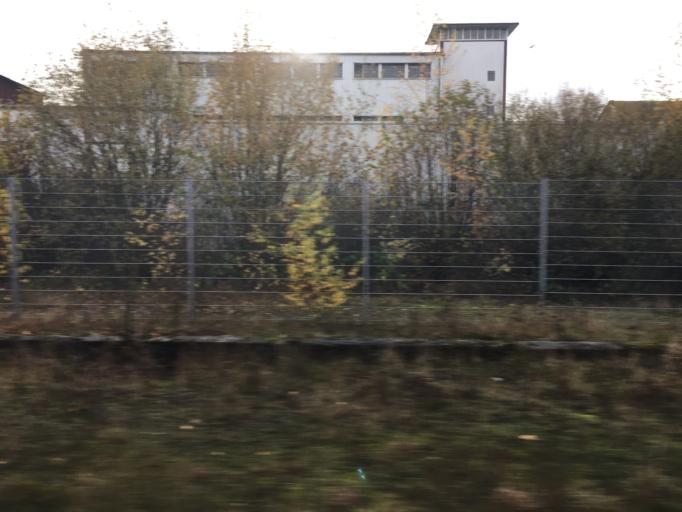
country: DE
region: North Rhine-Westphalia
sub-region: Regierungsbezirk Munster
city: Steinfurt
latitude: 52.1182
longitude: 7.4000
